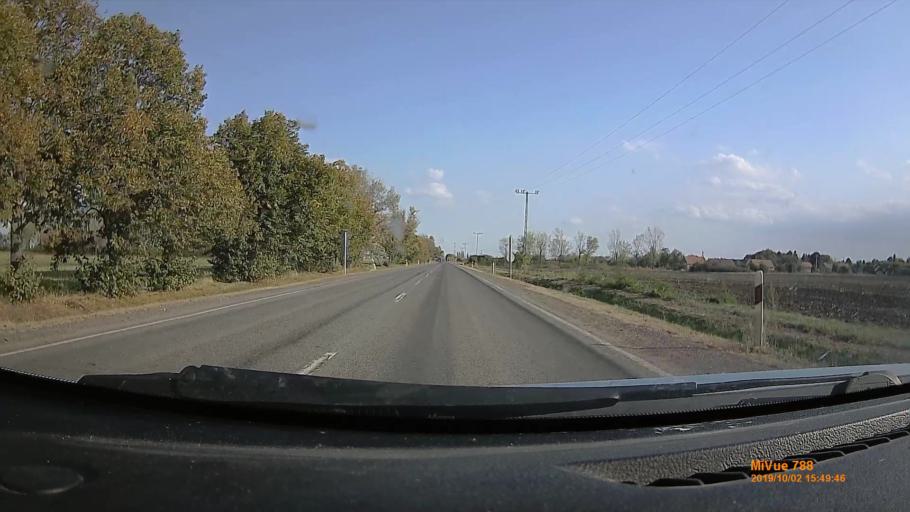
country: HU
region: Heves
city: Fuzesabony
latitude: 47.7711
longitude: 20.3806
